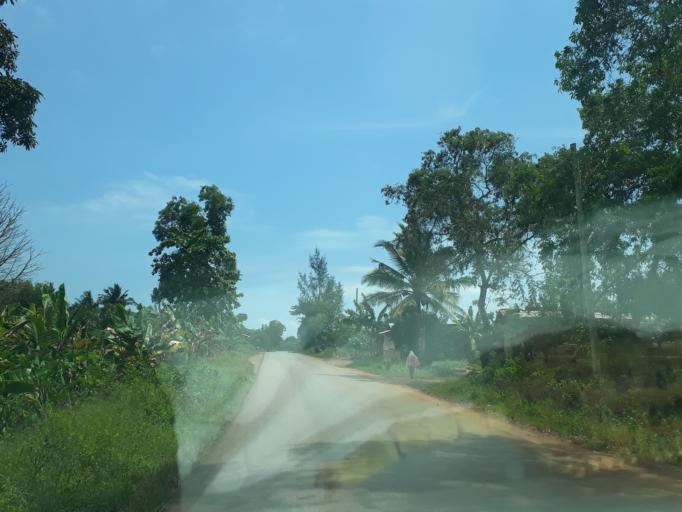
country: TZ
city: Kiwengwa
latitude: -5.9948
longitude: 39.3463
